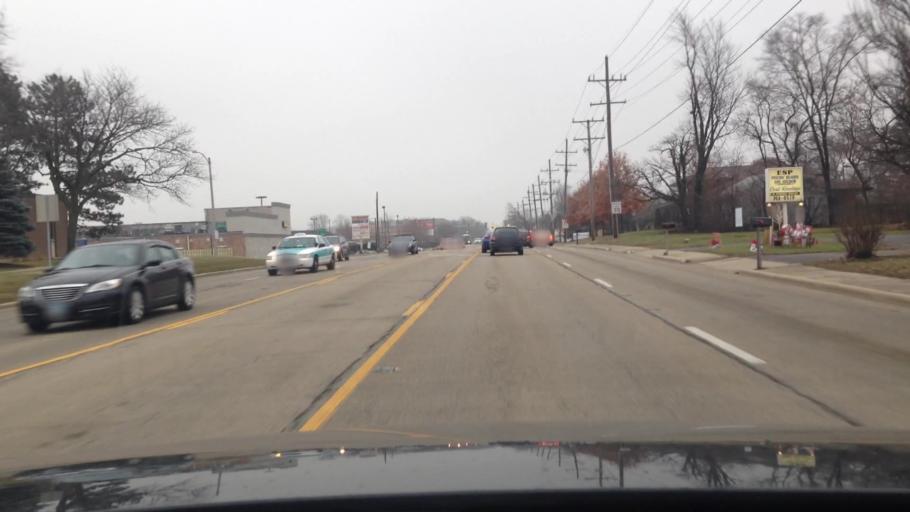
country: US
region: Illinois
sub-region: DuPage County
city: Westmont
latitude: 41.8137
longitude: -87.9761
